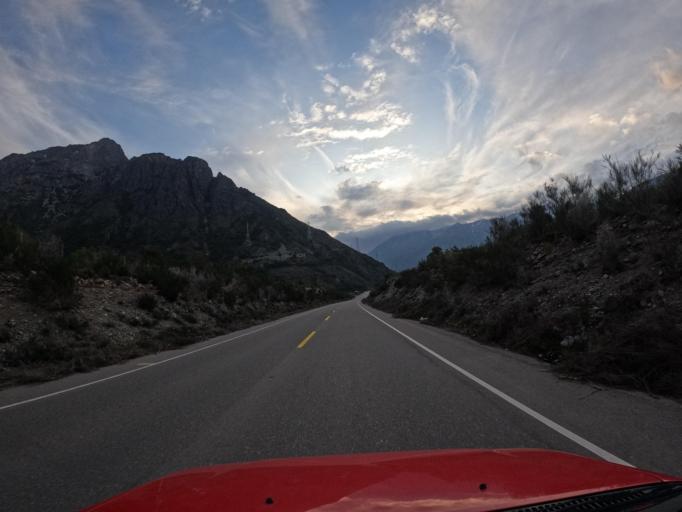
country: CL
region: Maule
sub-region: Provincia de Linares
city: Colbun
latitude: -35.7102
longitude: -71.0719
